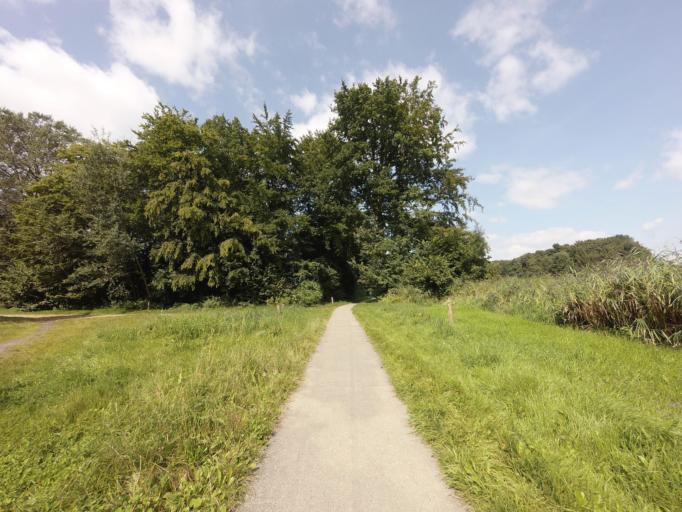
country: NL
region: Flevoland
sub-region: Gemeente Lelystad
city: Lelystad
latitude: 52.5093
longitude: 5.5223
